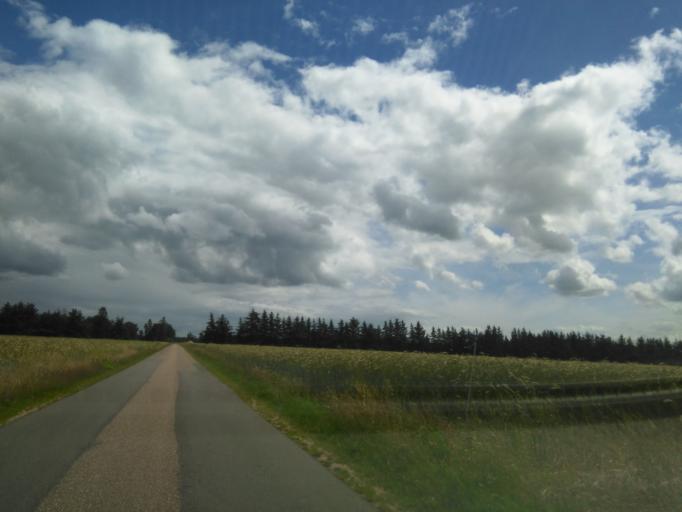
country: DK
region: Central Jutland
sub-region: Silkeborg Kommune
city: Virklund
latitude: 56.0389
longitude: 9.3903
